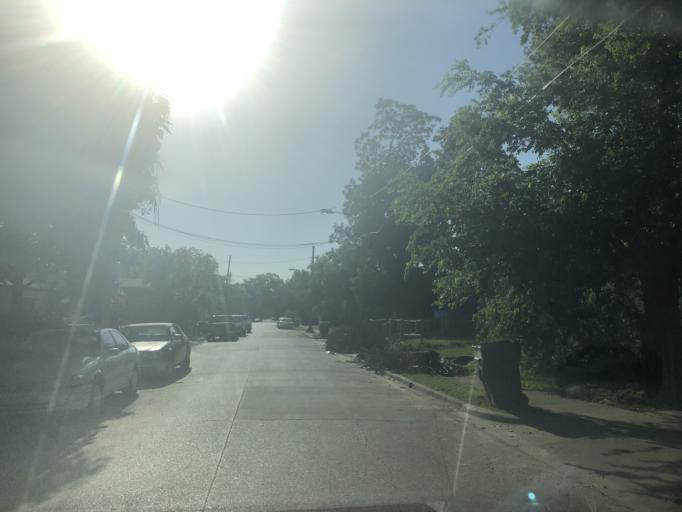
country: US
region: Texas
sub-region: Dallas County
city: Dallas
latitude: 32.7834
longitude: -96.8497
